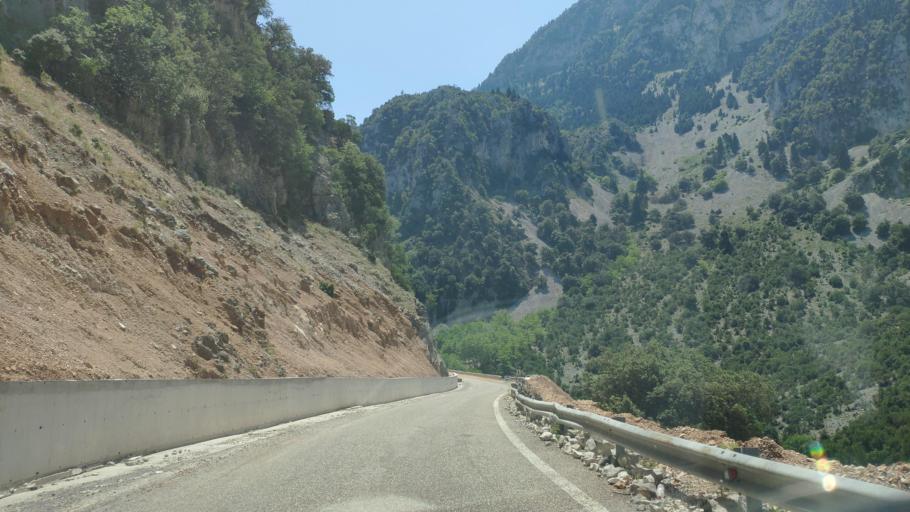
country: GR
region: West Greece
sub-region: Nomos Aitolias kai Akarnanias
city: Krikellos
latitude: 39.0071
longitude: 21.3682
